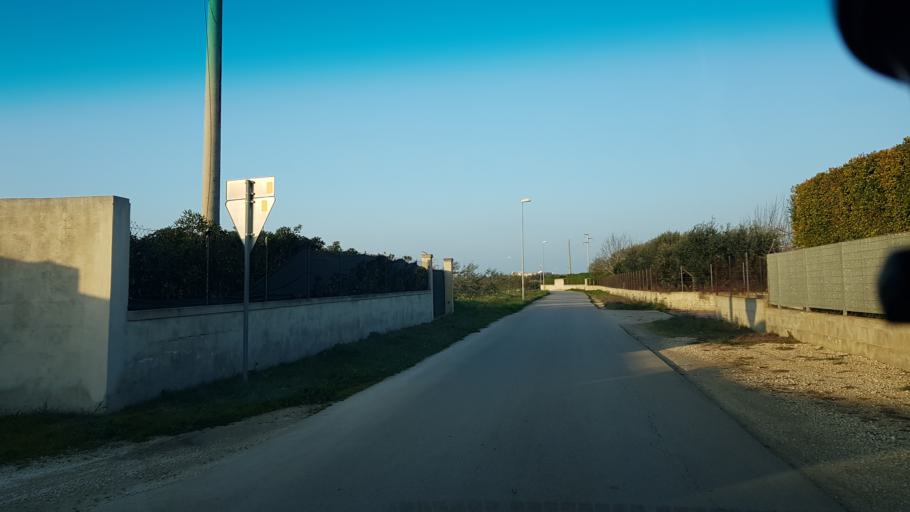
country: IT
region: Apulia
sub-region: Provincia di Brindisi
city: Mesagne
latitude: 40.5510
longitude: 17.7937
